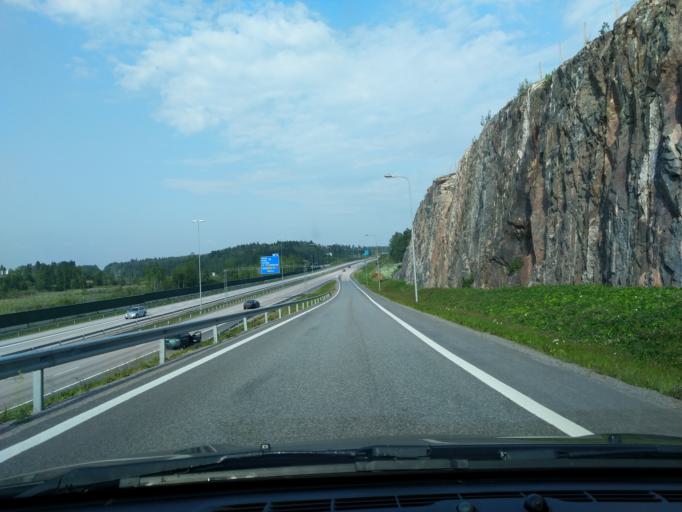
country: FI
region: Uusimaa
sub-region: Helsinki
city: Kirkkonummi
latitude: 60.1336
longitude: 24.5131
